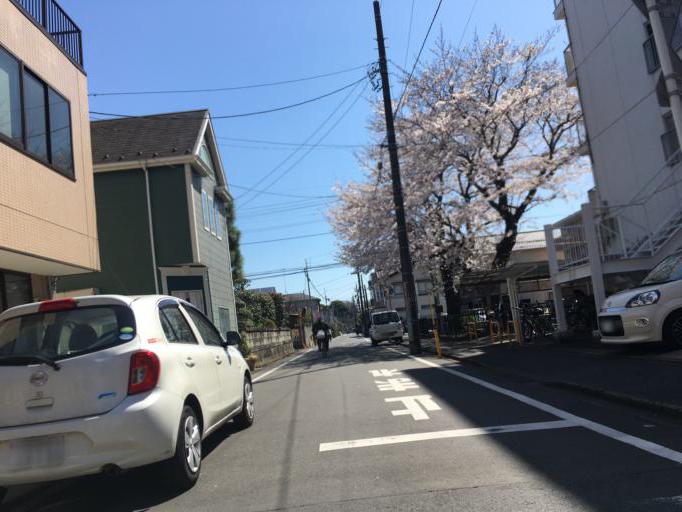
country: JP
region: Tokyo
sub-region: Machida-shi
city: Machida
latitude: 35.5752
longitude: 139.3772
